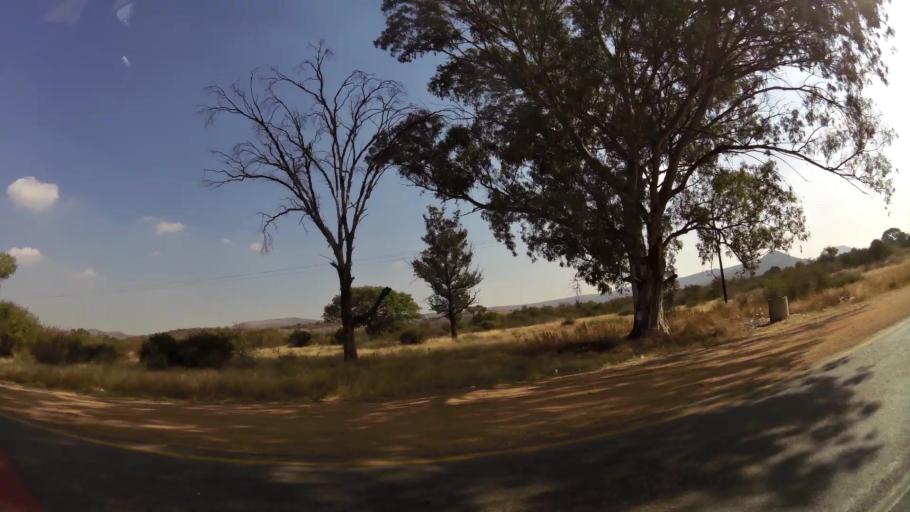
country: ZA
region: North-West
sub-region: Bojanala Platinum District Municipality
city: Rustenburg
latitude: -25.5155
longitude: 27.1009
